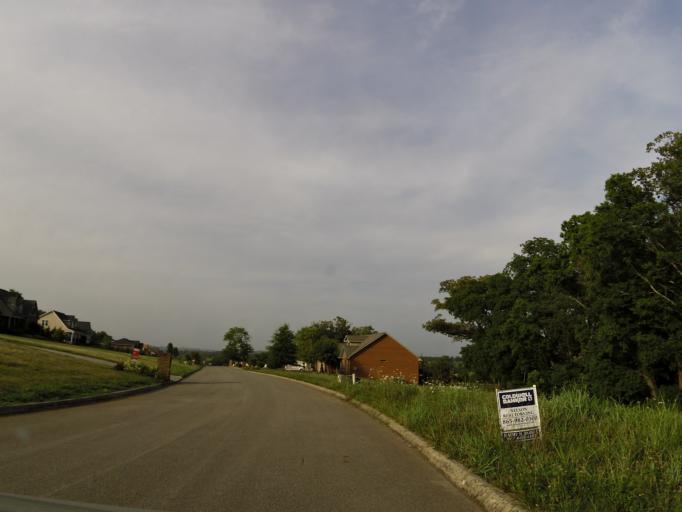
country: US
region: Tennessee
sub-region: Blount County
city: Wildwood
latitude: 35.8271
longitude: -83.8524
